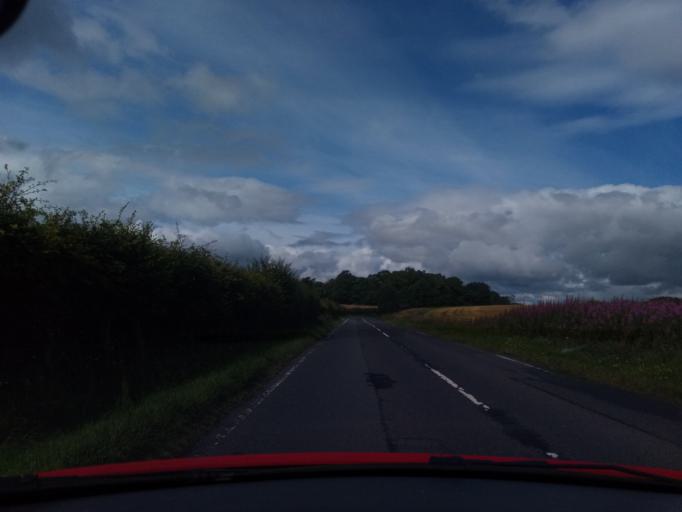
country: GB
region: Scotland
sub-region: The Scottish Borders
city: Lauder
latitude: 55.7171
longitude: -2.7137
